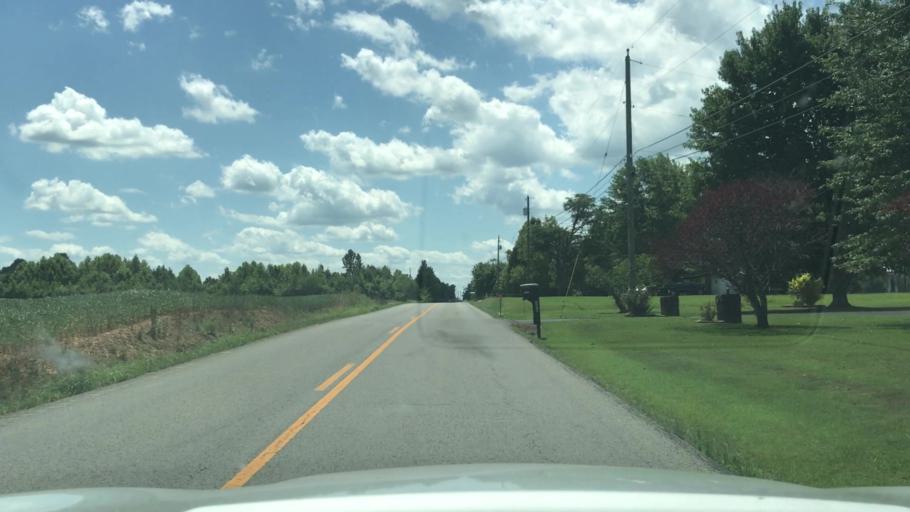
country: US
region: Kentucky
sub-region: Muhlenberg County
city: Greenville
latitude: 37.1699
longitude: -87.2449
